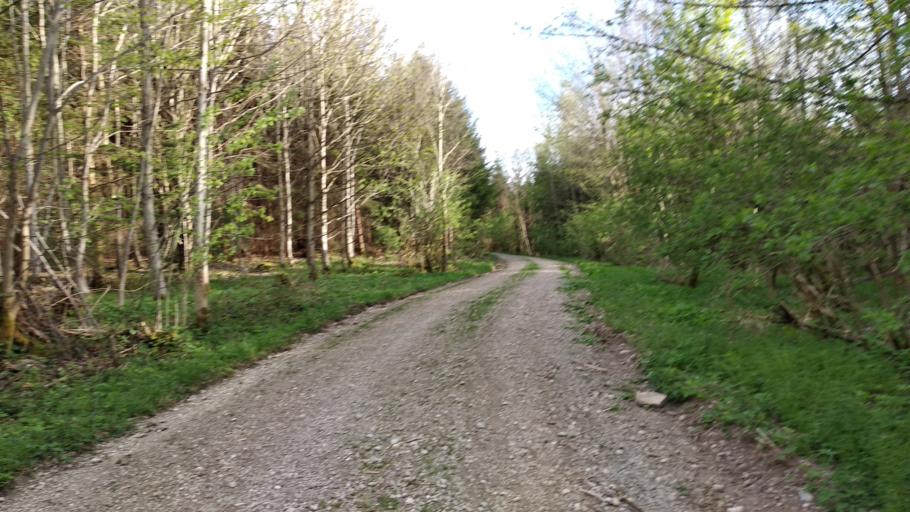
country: DE
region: Bavaria
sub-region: Swabia
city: Woringen
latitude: 47.9341
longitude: 10.1932
